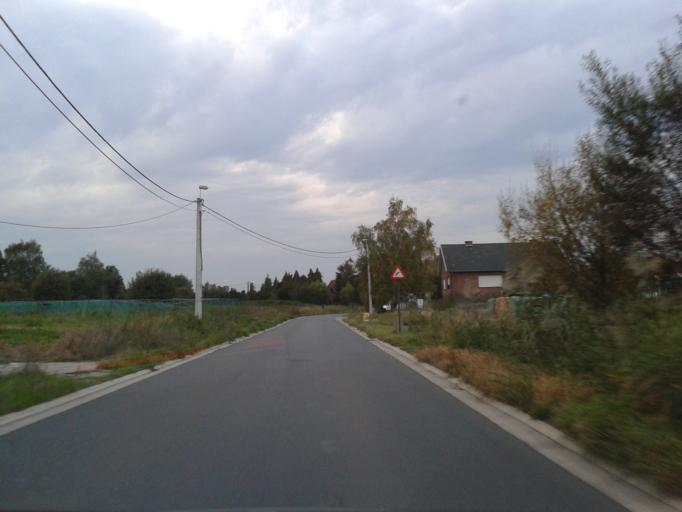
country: BE
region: Flanders
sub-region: Provincie Oost-Vlaanderen
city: Lebbeke
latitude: 50.9768
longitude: 4.0991
